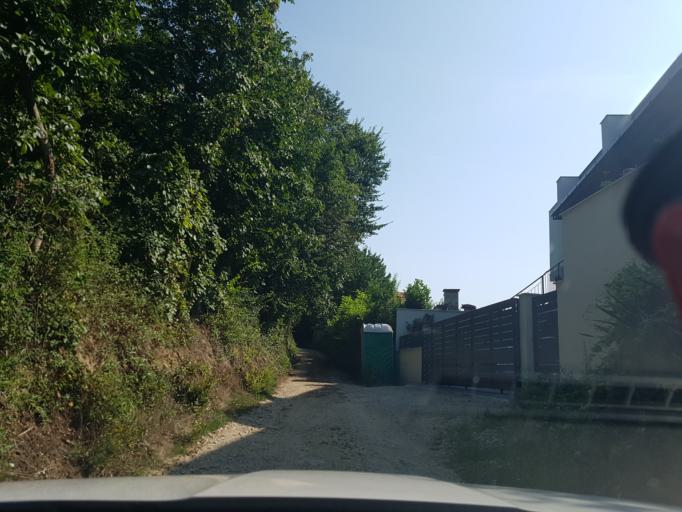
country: HU
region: Veszprem
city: Balatonalmadi
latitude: 46.9974
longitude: 17.9833
